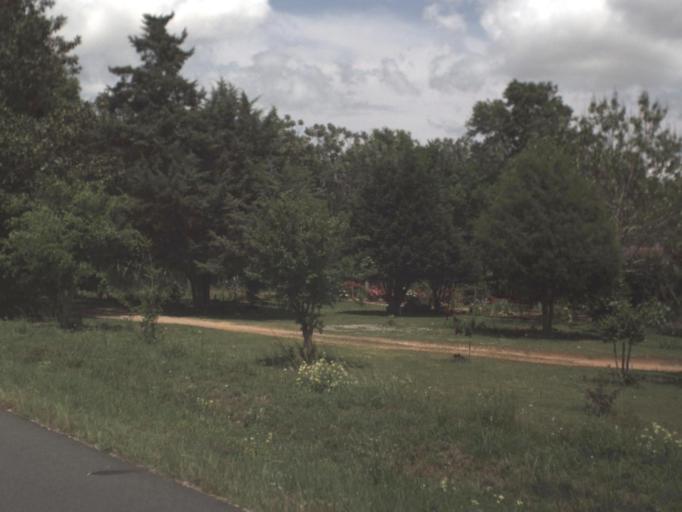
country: US
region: Florida
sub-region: Escambia County
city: Century
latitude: 30.9323
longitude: -87.1572
